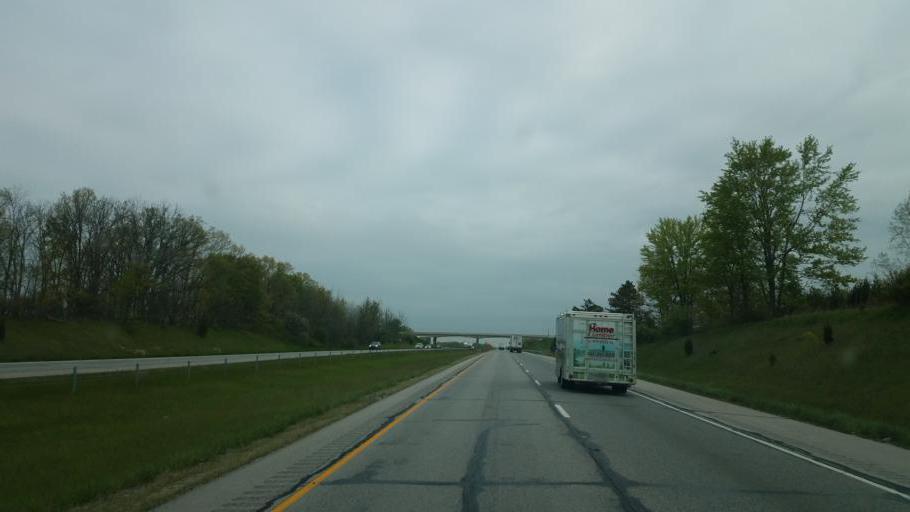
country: US
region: Indiana
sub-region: DeKalb County
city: Garrett
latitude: 41.2770
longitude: -85.0869
